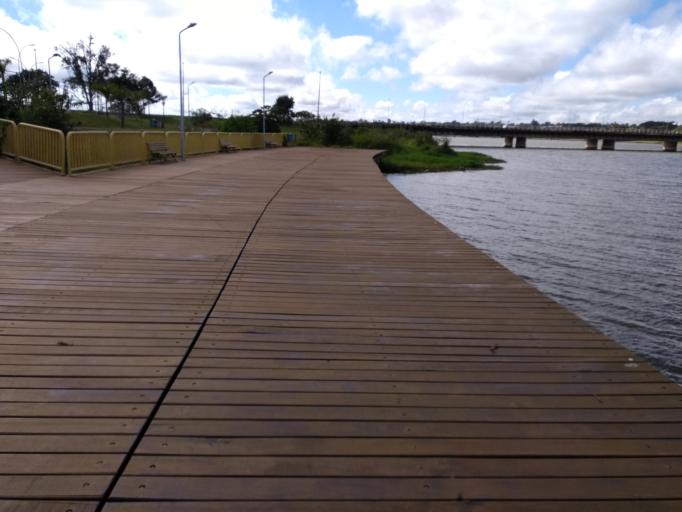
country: BR
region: Federal District
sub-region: Brasilia
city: Brasilia
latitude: -15.8385
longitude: -47.9003
